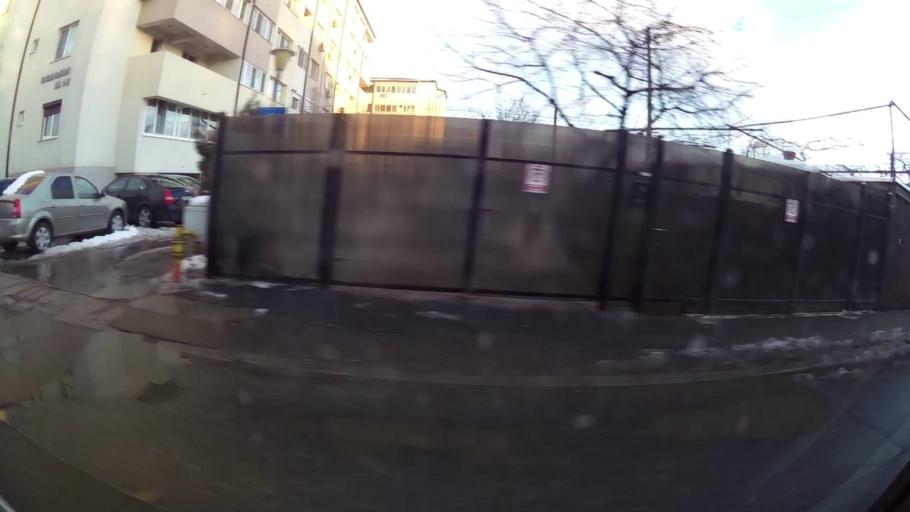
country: RO
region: Ilfov
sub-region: Comuna Popesti-Leordeni
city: Popesti-Leordeni
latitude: 44.3760
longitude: 26.1455
